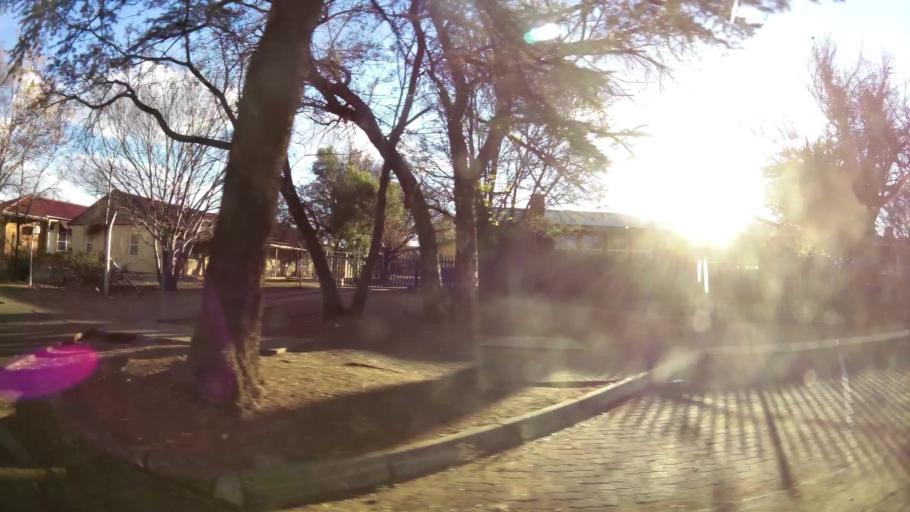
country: ZA
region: North-West
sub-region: Dr Kenneth Kaunda District Municipality
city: Potchefstroom
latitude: -26.7266
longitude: 27.0898
